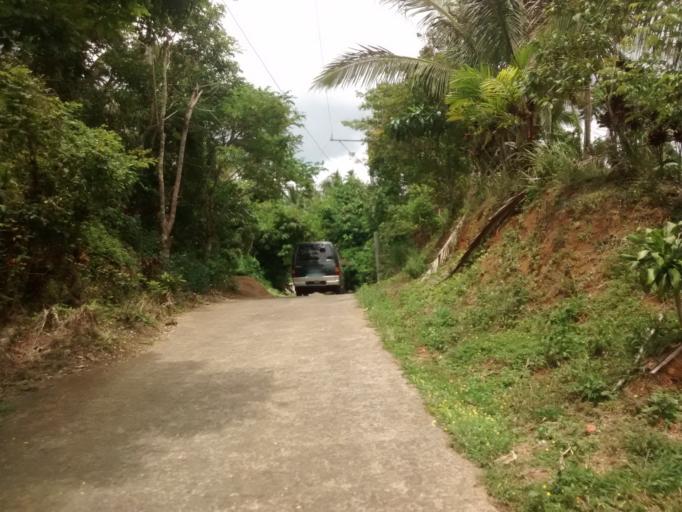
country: PH
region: Calabarzon
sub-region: Province of Quezon
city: Lucban
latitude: 14.1557
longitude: 121.5552
